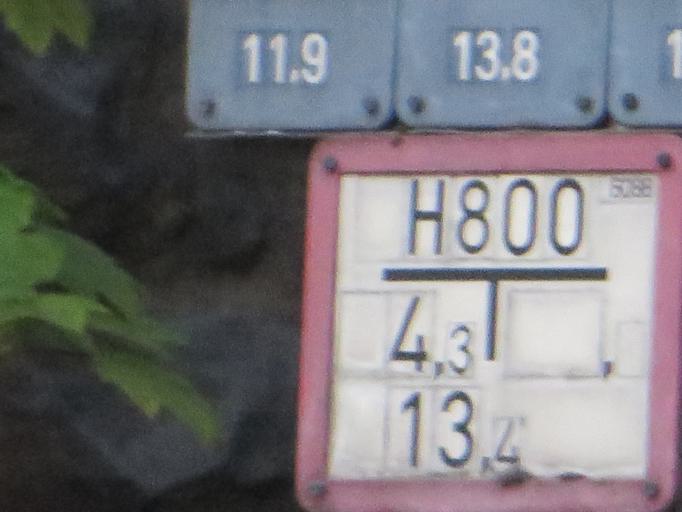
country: DE
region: North Rhine-Westphalia
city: Witten
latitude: 51.4310
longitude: 7.3359
